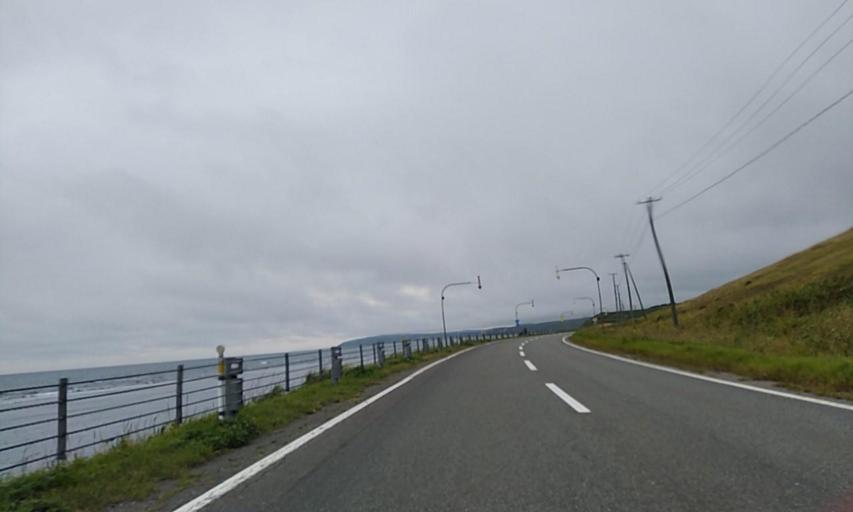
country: JP
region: Hokkaido
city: Makubetsu
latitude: 45.5063
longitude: 141.9633
